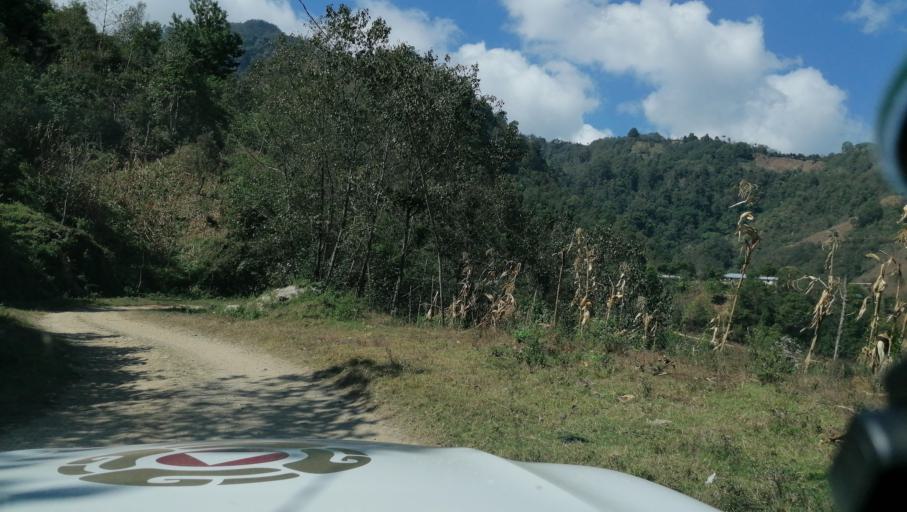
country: GT
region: San Marcos
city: Tacana
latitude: 15.2070
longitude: -92.2071
